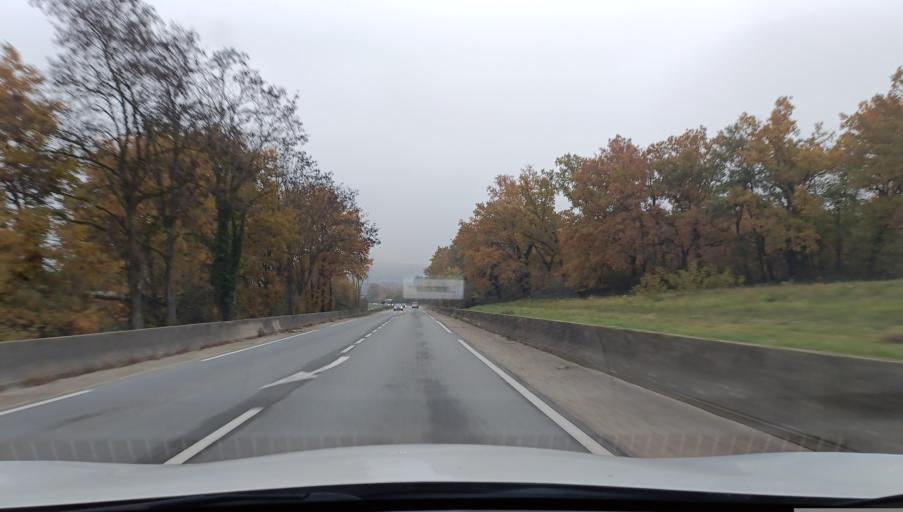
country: FR
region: Rhone-Alpes
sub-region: Departement de l'Isere
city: Pont-Eveque
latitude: 45.5290
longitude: 4.9294
